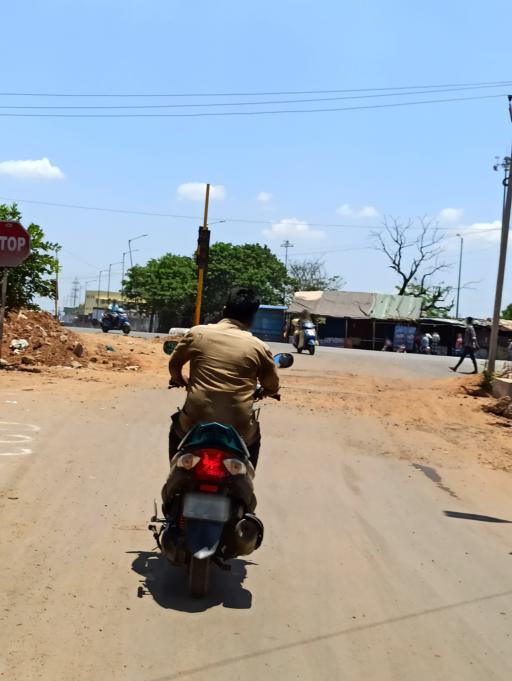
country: IN
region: Tamil Nadu
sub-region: Thiruvallur
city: Chinnasekkadu
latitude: 13.1634
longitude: 80.2283
